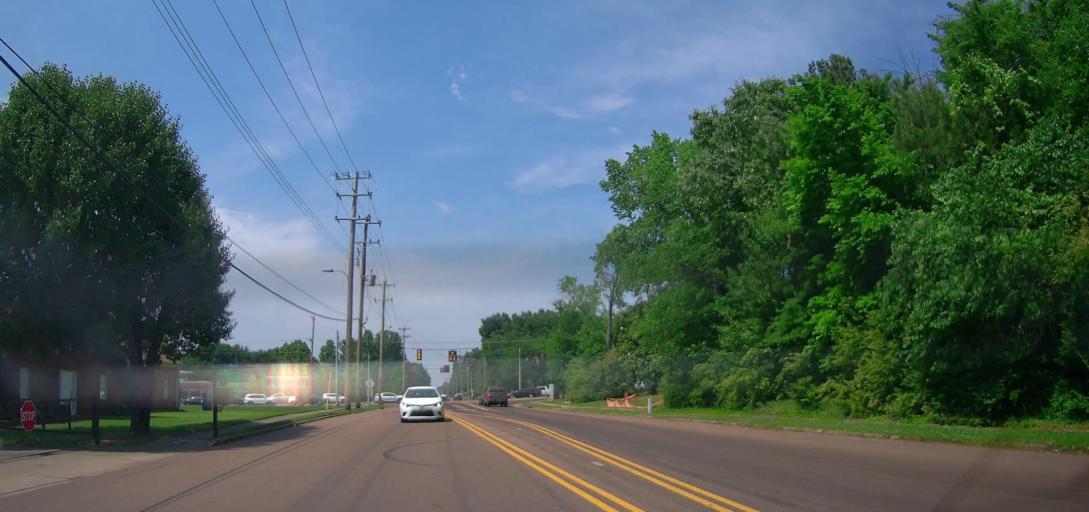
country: US
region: Mississippi
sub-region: De Soto County
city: Olive Branch
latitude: 35.0197
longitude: -89.8223
